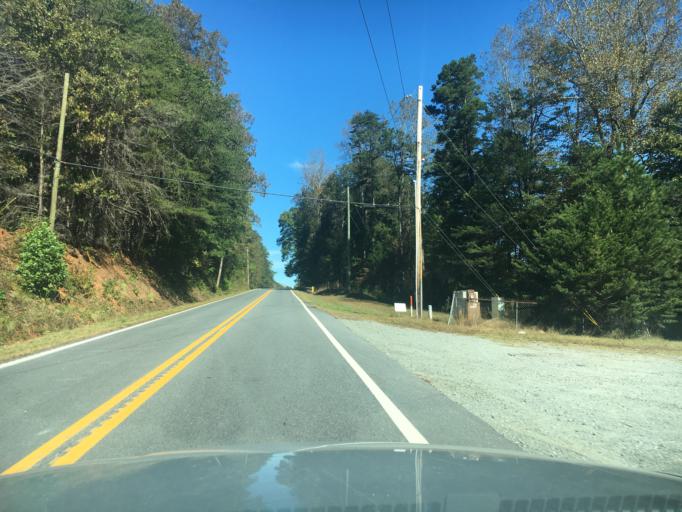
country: US
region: North Carolina
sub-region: Rutherford County
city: Spindale
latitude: 35.5077
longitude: -81.8562
